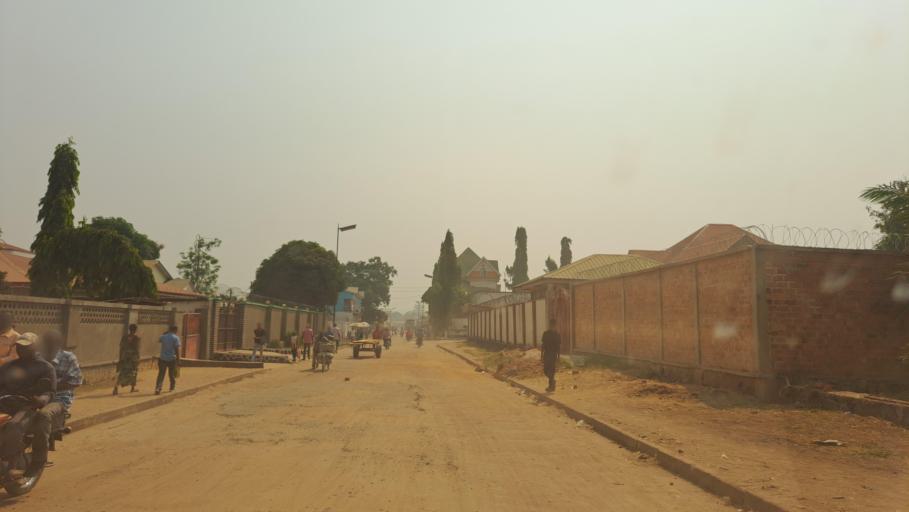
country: CD
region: Kasai-Occidental
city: Kananga
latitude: -5.8985
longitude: 22.4068
